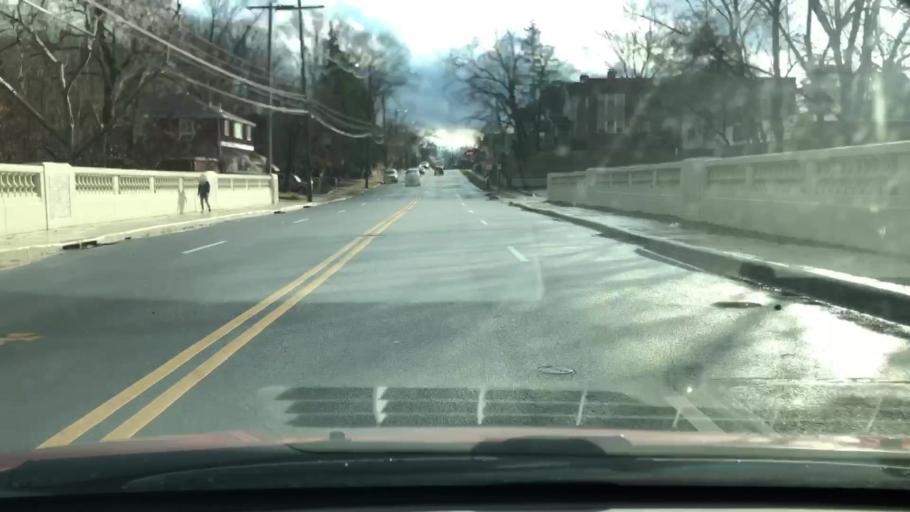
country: US
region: Ohio
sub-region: Franklin County
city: Grandview Heights
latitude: 40.0191
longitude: -83.0020
